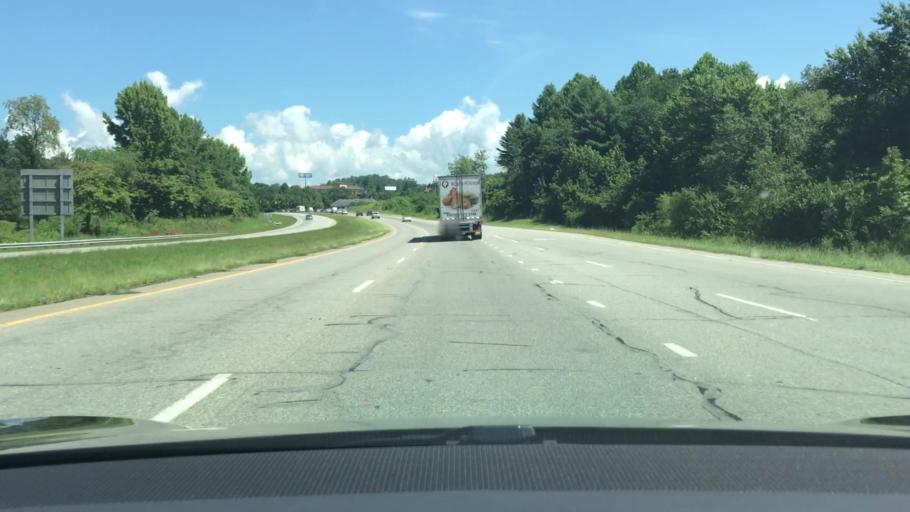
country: US
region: North Carolina
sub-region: Macon County
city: Franklin
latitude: 35.1785
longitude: -83.3567
